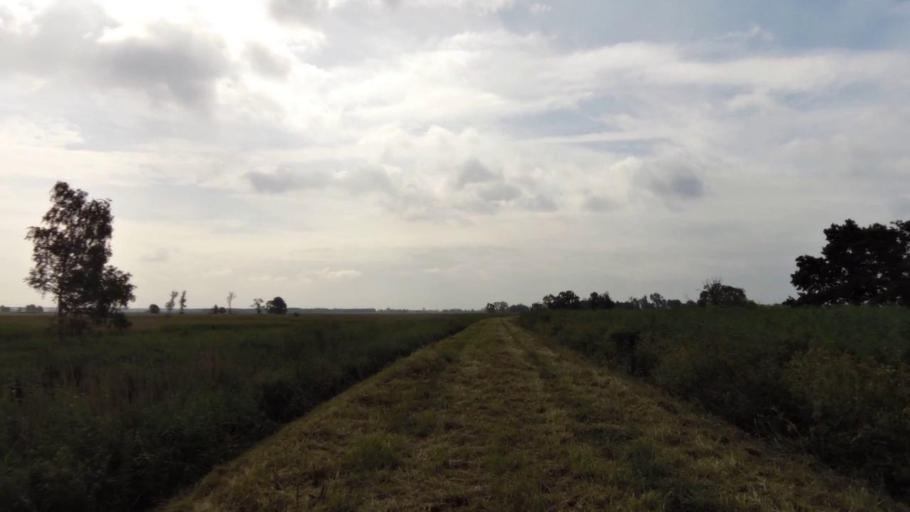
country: PL
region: West Pomeranian Voivodeship
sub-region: Powiat policki
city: Police
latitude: 53.5358
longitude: 14.6789
